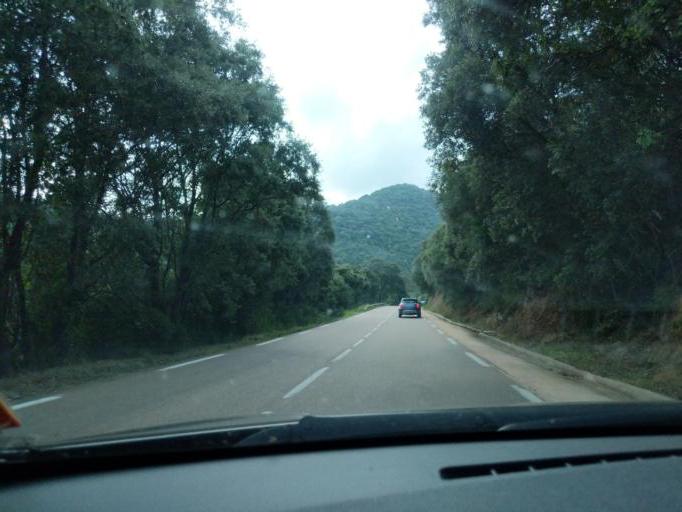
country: FR
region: Corsica
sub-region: Departement de la Corse-du-Sud
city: Sartene
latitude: 41.5781
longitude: 8.9523
